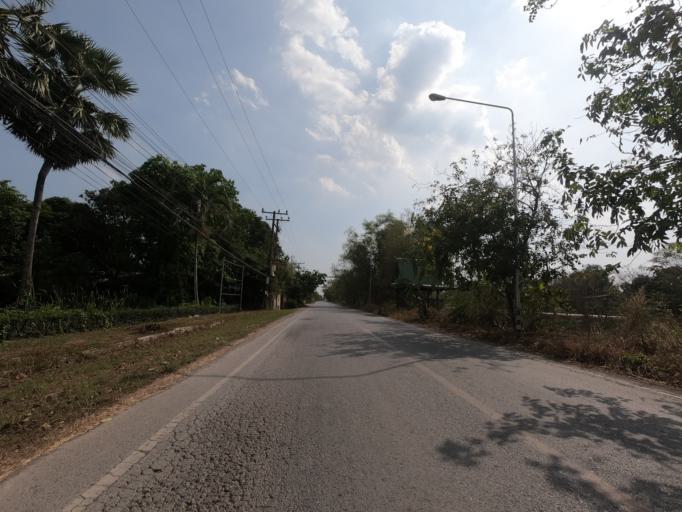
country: TH
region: Pathum Thani
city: Nong Suea
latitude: 14.1309
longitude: 100.8465
